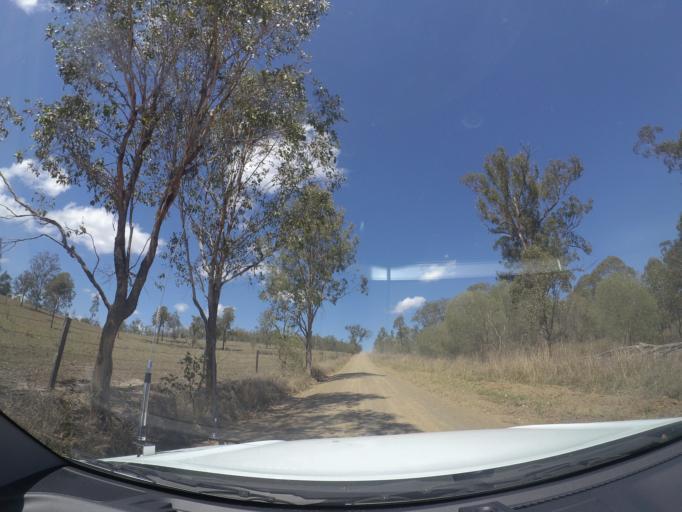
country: AU
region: Queensland
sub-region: Logan
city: Cedar Vale
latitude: -27.8537
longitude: 152.8860
